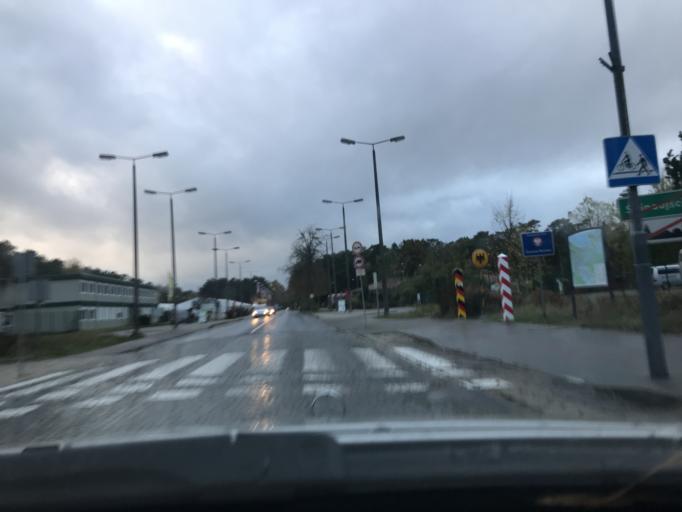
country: PL
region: West Pomeranian Voivodeship
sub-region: Swinoujscie
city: Swinoujscie
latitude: 53.9219
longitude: 14.2177
